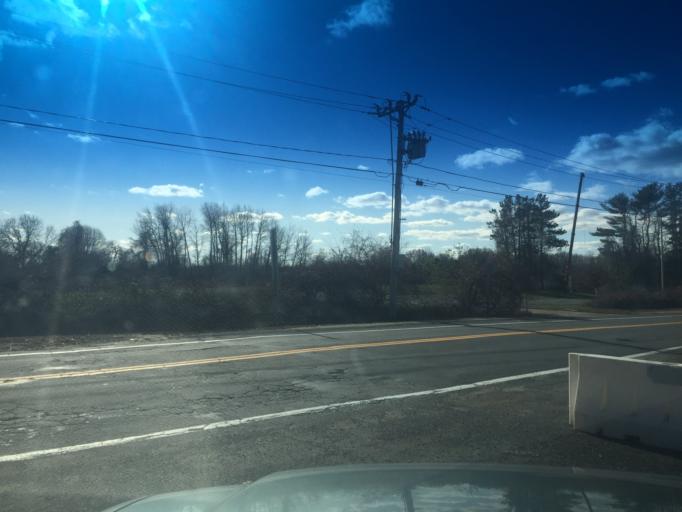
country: US
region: Rhode Island
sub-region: Providence County
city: Greenville
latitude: 41.8636
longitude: -71.5763
